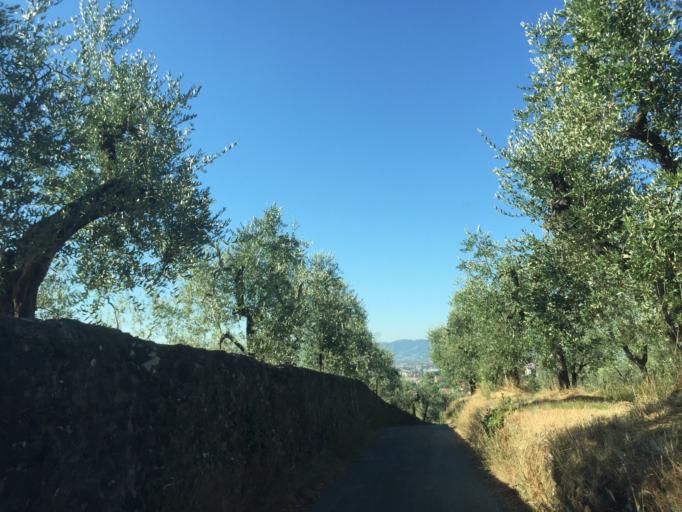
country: IT
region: Tuscany
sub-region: Provincia di Pistoia
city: Pistoia
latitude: 43.9574
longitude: 10.9412
